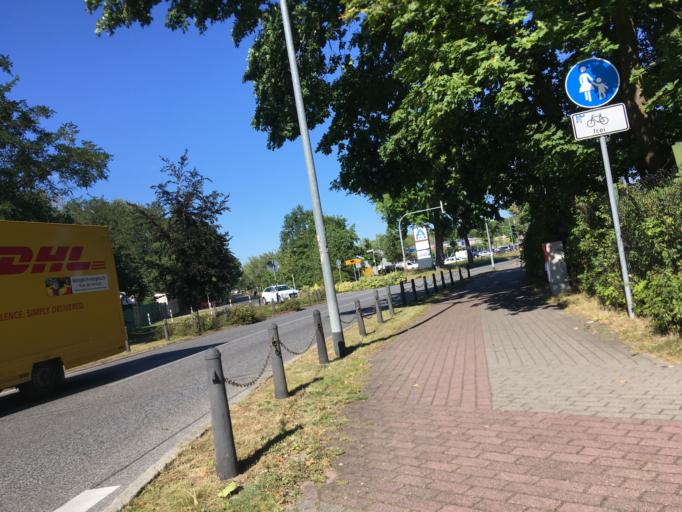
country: DE
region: Brandenburg
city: Schulzendorf
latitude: 52.3629
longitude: 13.5898
